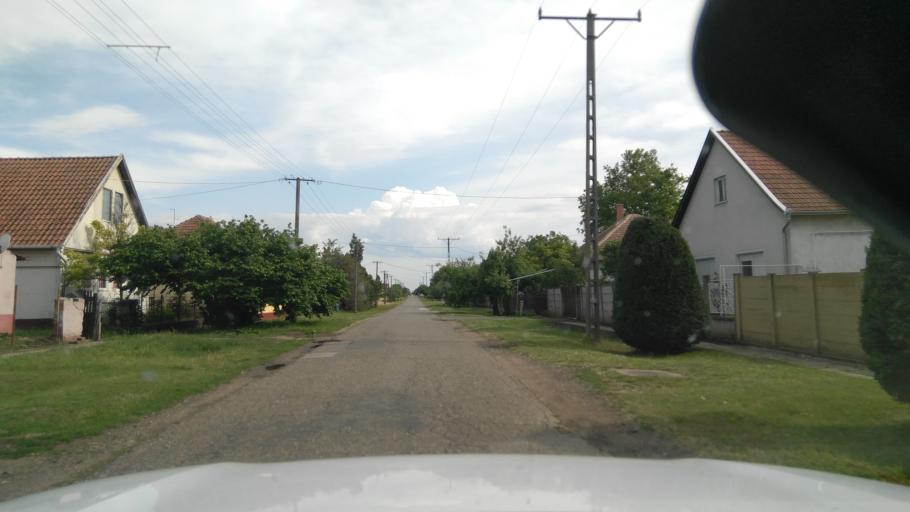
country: HU
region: Bekes
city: Ujkigyos
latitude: 46.5867
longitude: 21.0339
